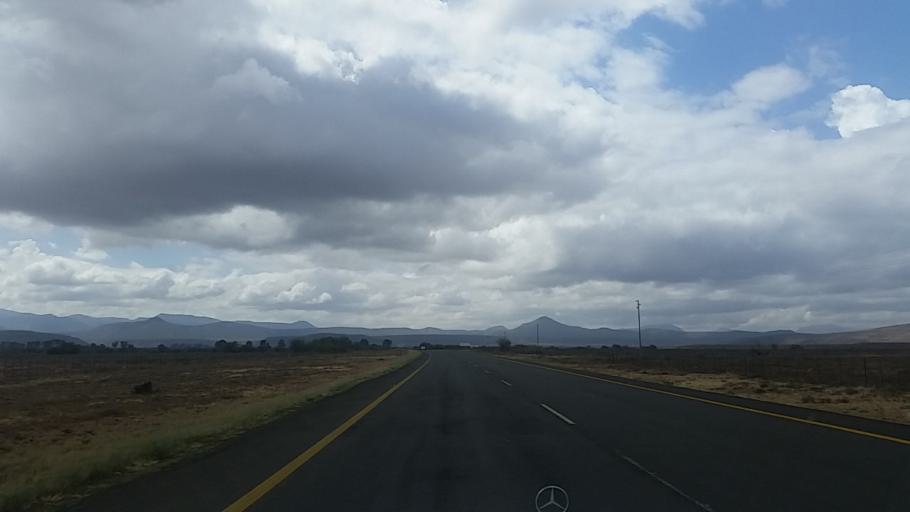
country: ZA
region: Eastern Cape
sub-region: Cacadu District Municipality
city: Graaff-Reinet
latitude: -32.2051
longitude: 24.5505
